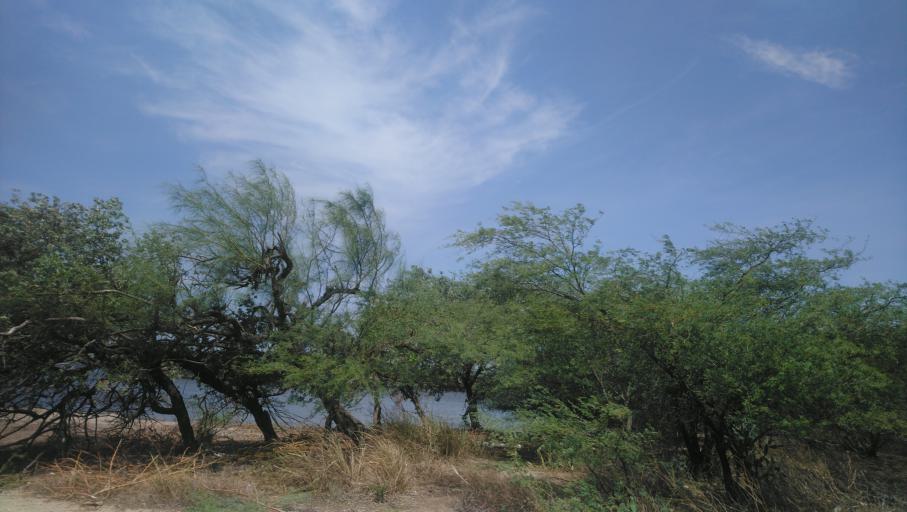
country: MX
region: Oaxaca
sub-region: Salina Cruz
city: Salina Cruz
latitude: 16.1964
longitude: -95.1195
